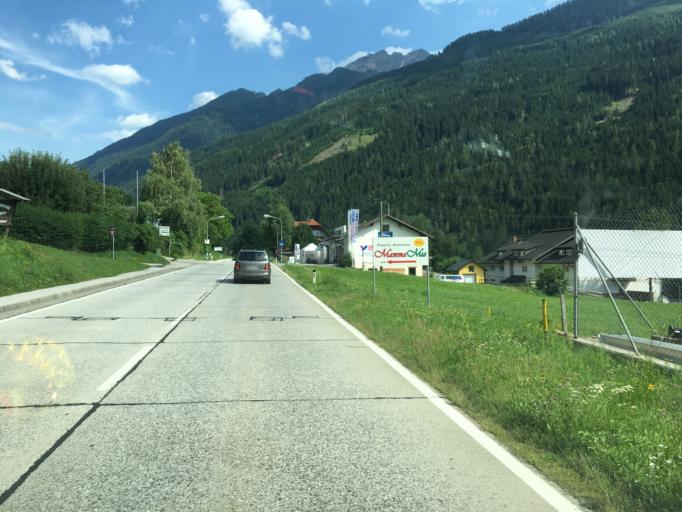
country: AT
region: Carinthia
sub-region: Politischer Bezirk Spittal an der Drau
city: Flattach
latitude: 46.9346
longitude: 13.1118
